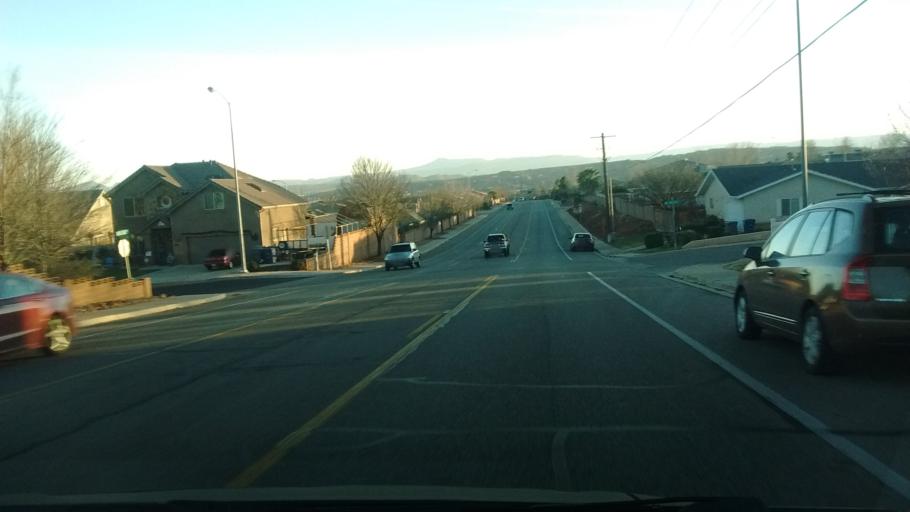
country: US
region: Utah
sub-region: Washington County
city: Washington
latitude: 37.1096
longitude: -113.5318
